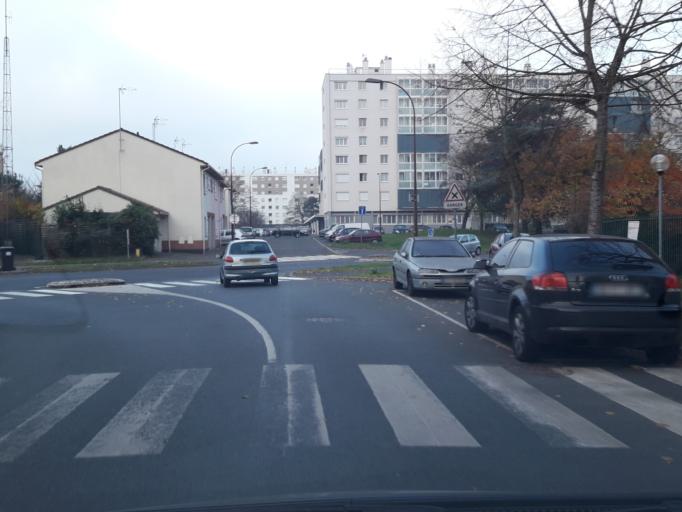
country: FR
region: Ile-de-France
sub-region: Departement de l'Essonne
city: Fleury-Merogis
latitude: 48.6399
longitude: 2.3492
